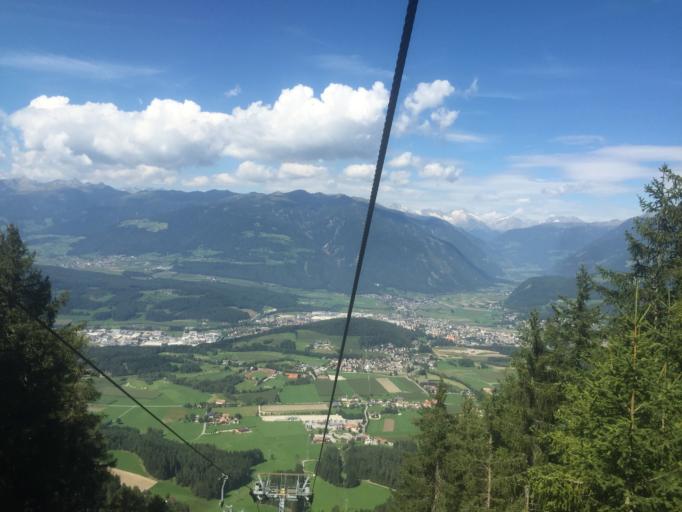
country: IT
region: Trentino-Alto Adige
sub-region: Bolzano
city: Riscone
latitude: 46.7572
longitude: 11.9481
